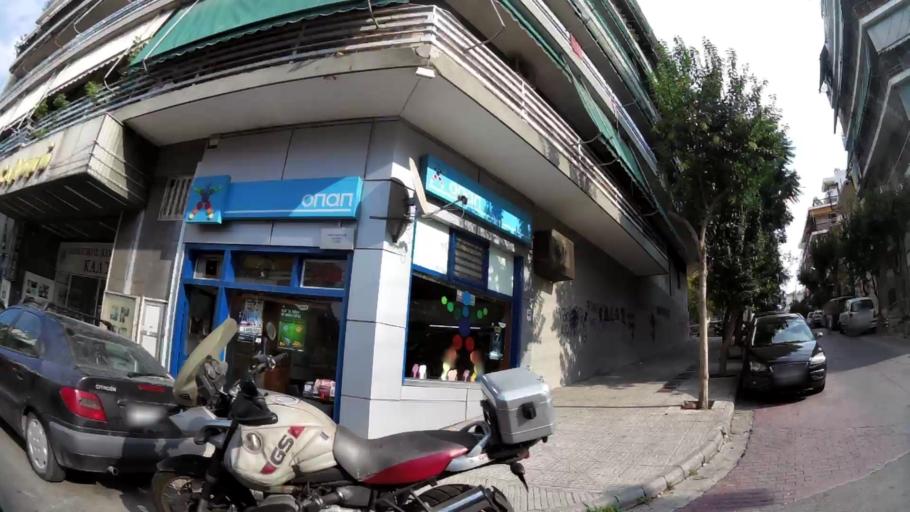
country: GR
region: Attica
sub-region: Nomarchia Athinas
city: Nea Smyrni
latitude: 37.9593
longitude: 23.7137
